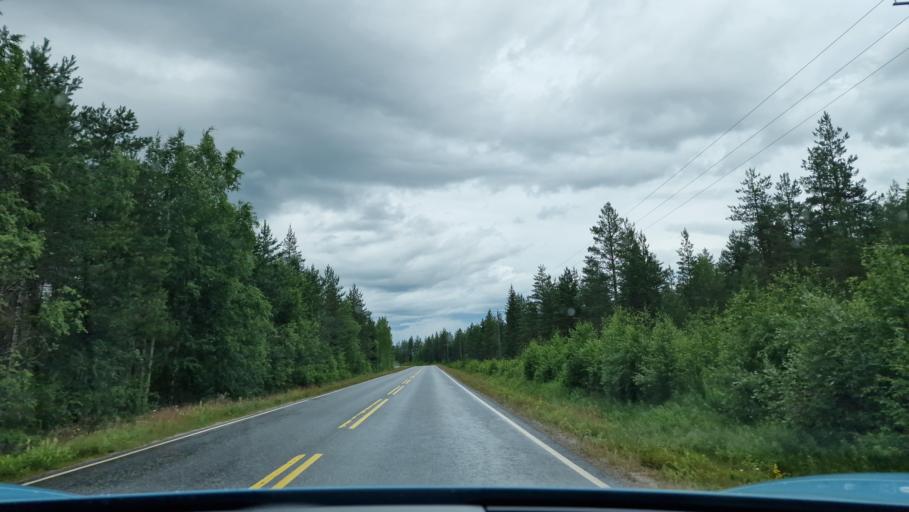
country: FI
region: Southern Ostrobothnia
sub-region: Jaerviseutu
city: Soini
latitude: 62.7346
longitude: 24.4202
